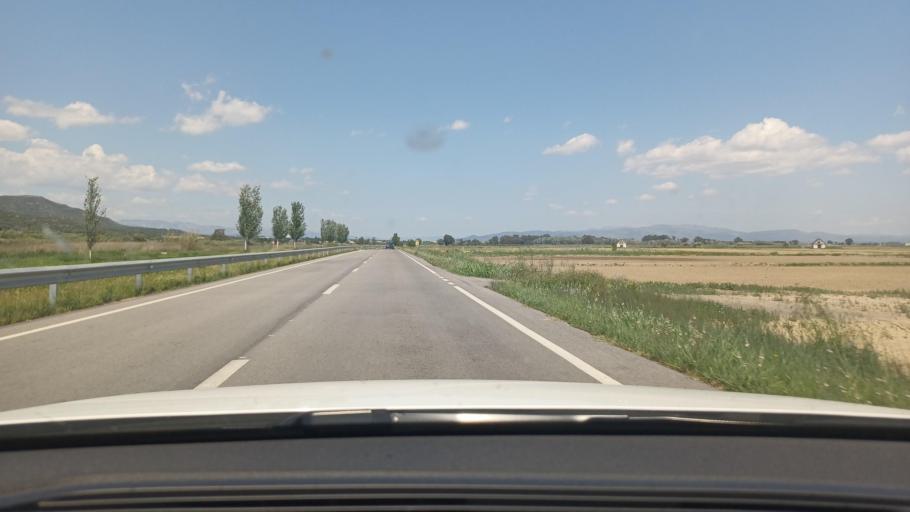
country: ES
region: Catalonia
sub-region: Provincia de Tarragona
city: Sant Carles de la Rapita
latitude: 40.6546
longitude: 0.5948
